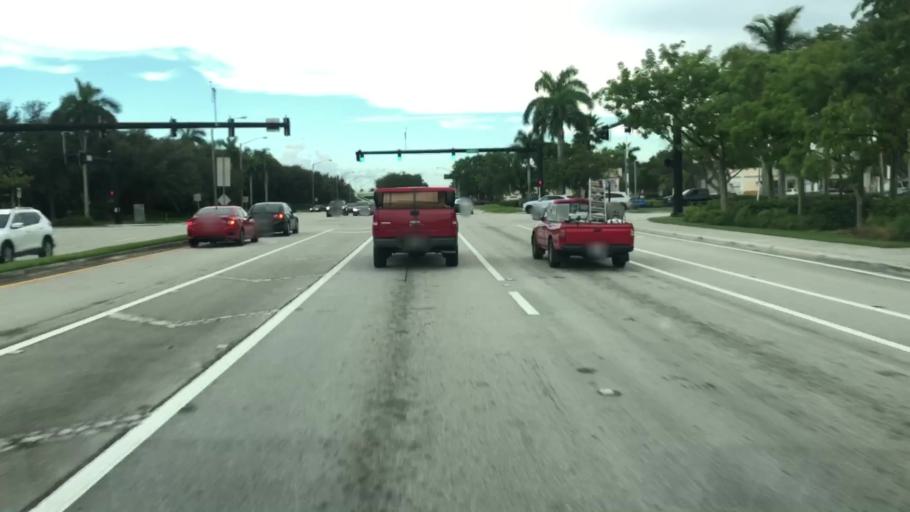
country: US
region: Florida
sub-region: Broward County
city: Coral Springs
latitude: 26.3069
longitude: -80.2789
